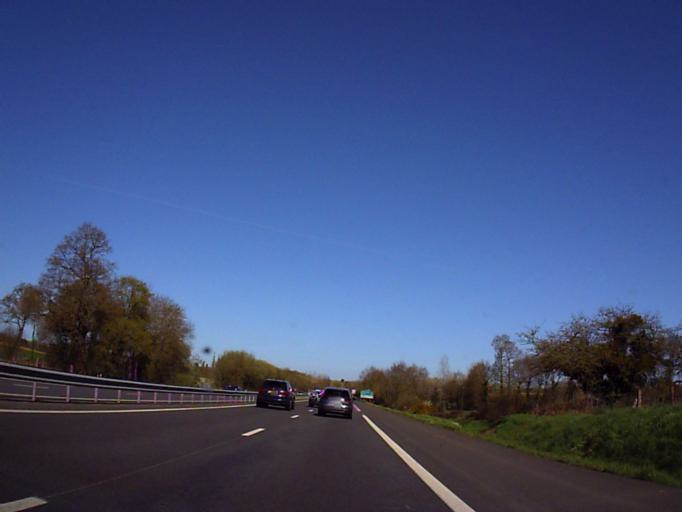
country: FR
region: Brittany
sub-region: Departement des Cotes-d'Armor
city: Broons
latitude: 48.3272
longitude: -2.2598
